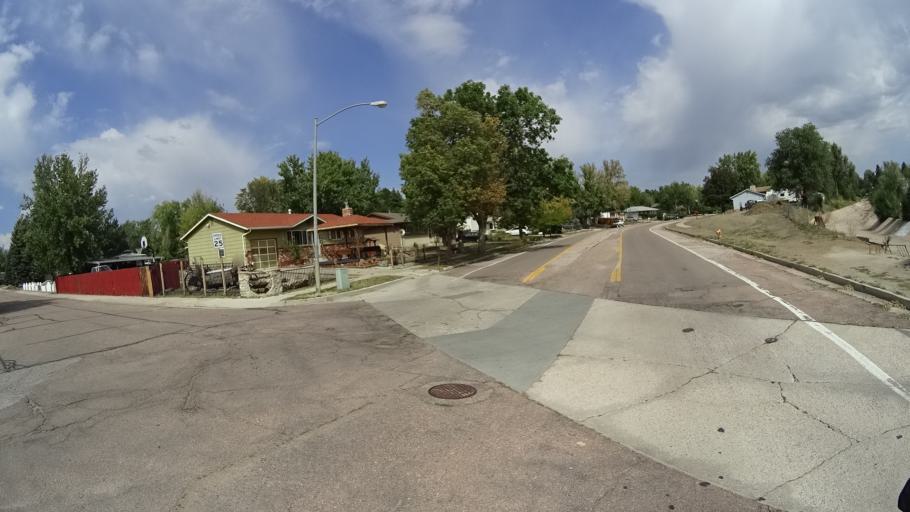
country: US
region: Colorado
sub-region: El Paso County
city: Cimarron Hills
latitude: 38.8492
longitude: -104.7387
